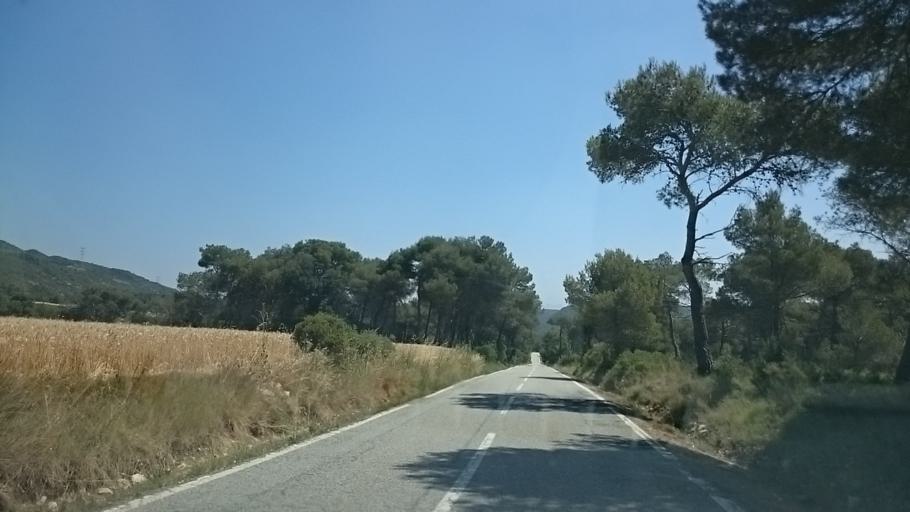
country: ES
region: Catalonia
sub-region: Provincia de Barcelona
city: Bellprat
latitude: 41.4571
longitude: 1.4571
